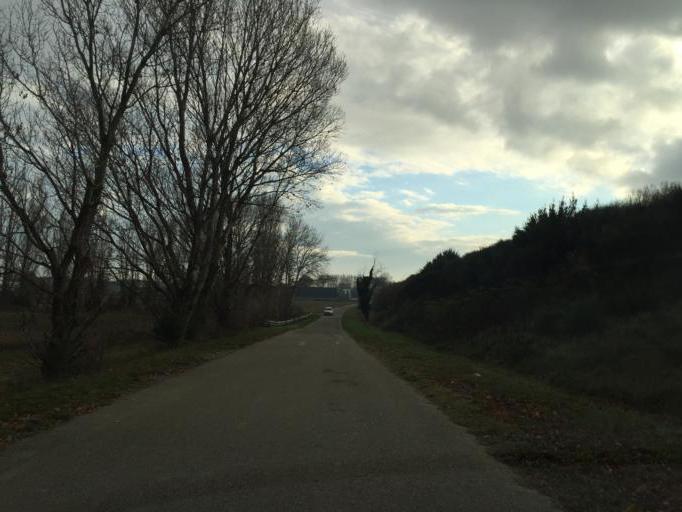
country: FR
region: Provence-Alpes-Cote d'Azur
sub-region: Departement du Vaucluse
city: Courthezon
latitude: 44.1014
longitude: 4.8824
